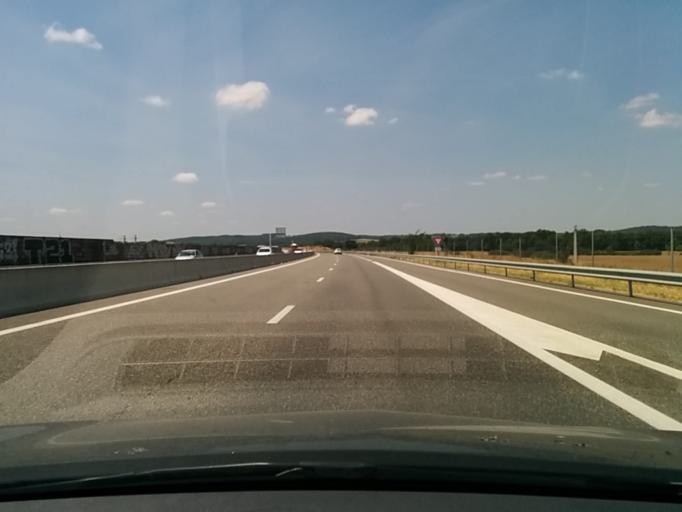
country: FR
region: Midi-Pyrenees
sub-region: Departement de la Haute-Garonne
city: Leguevin
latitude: 43.5825
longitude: 1.2150
